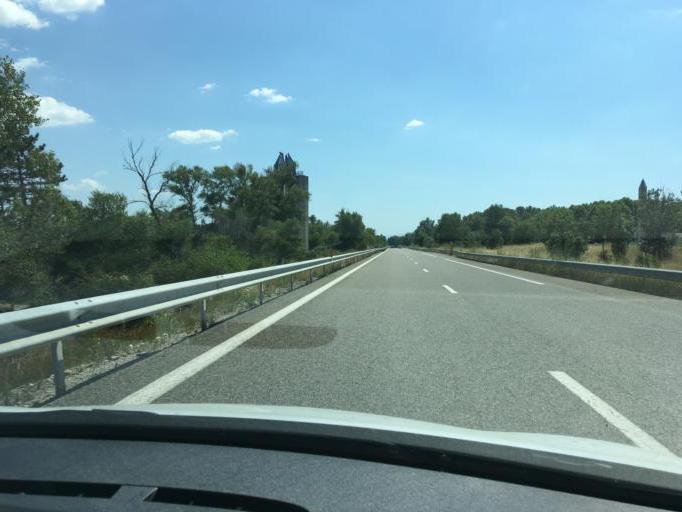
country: FR
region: Provence-Alpes-Cote d'Azur
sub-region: Departement des Alpes-de-Haute-Provence
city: Volx
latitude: 43.8444
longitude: 5.8501
